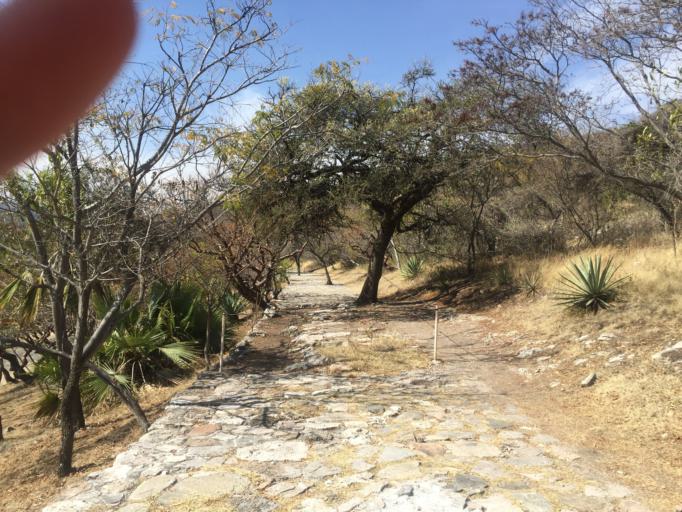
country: MX
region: Morelos
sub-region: Miacatlan
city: Xochicalco (Cirenio Longares)
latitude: 18.8031
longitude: -99.2915
